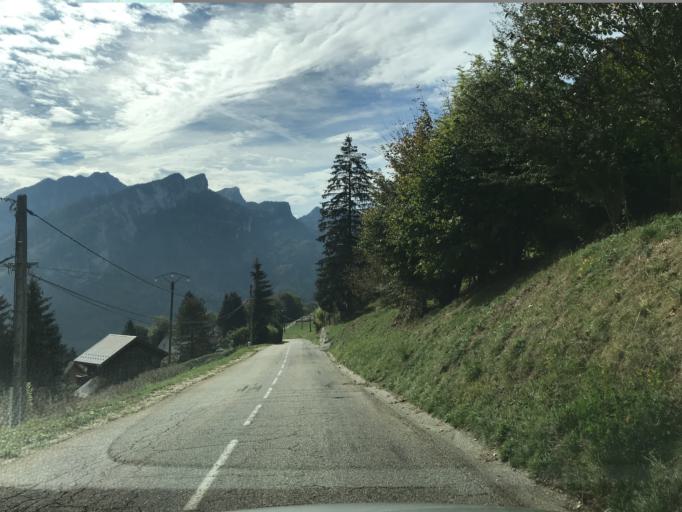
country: FR
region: Rhone-Alpes
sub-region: Departement de la Savoie
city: Les Echelles
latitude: 45.4372
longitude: 5.8310
